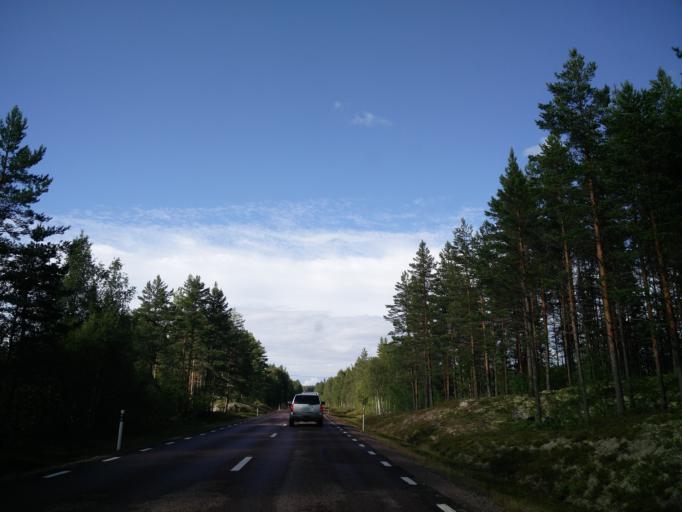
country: SE
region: Vaermland
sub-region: Hagfors Kommun
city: Ekshaerad
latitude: 60.4662
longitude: 13.3005
